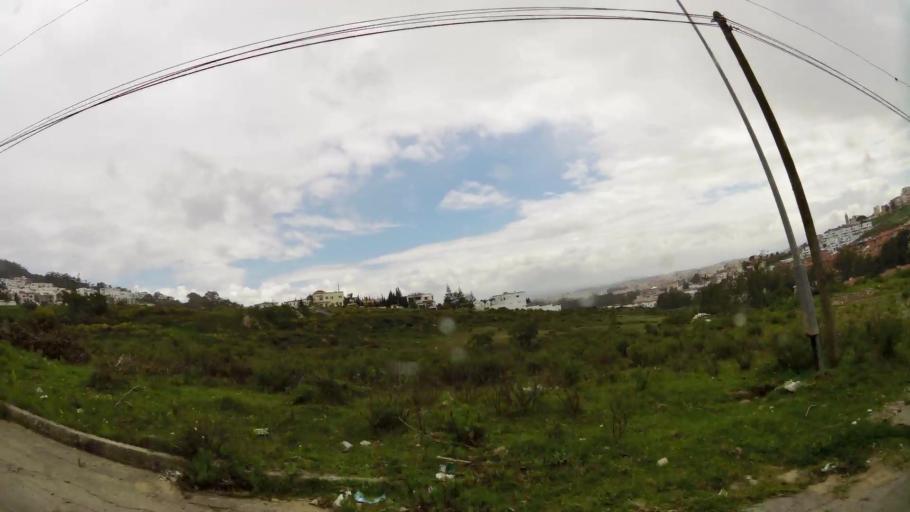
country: MA
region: Tanger-Tetouan
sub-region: Tanger-Assilah
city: Boukhalef
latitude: 35.7797
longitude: -5.8651
